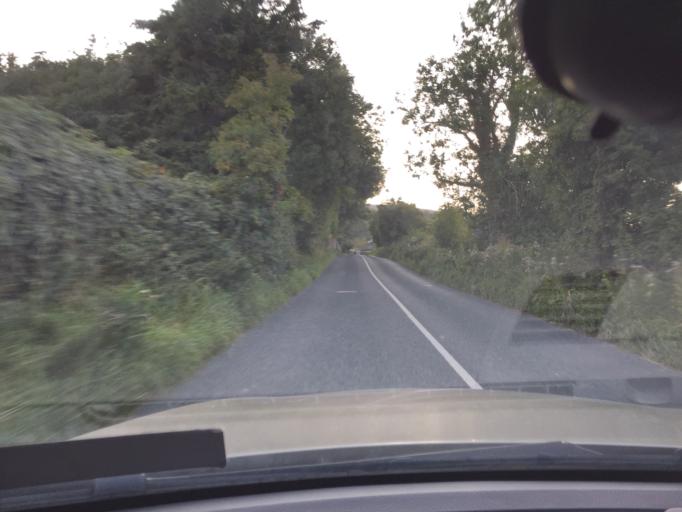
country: IE
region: Leinster
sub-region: Wicklow
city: Enniskerry
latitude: 53.1936
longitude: -6.1881
